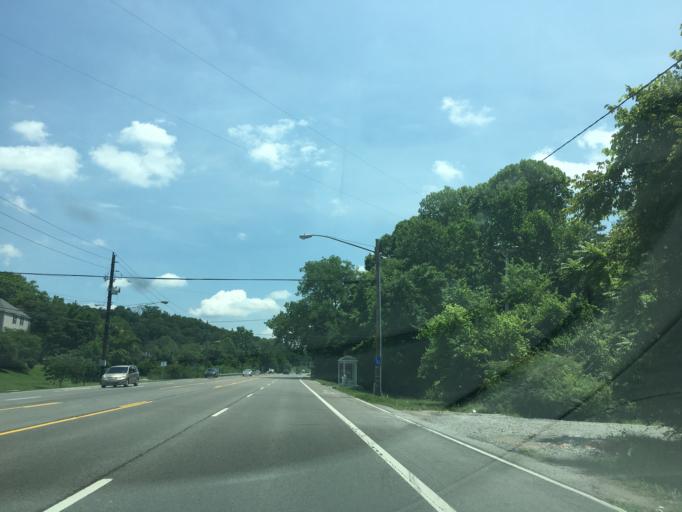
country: US
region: Tennessee
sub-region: Davidson County
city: Belle Meade
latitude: 36.0772
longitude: -86.9126
